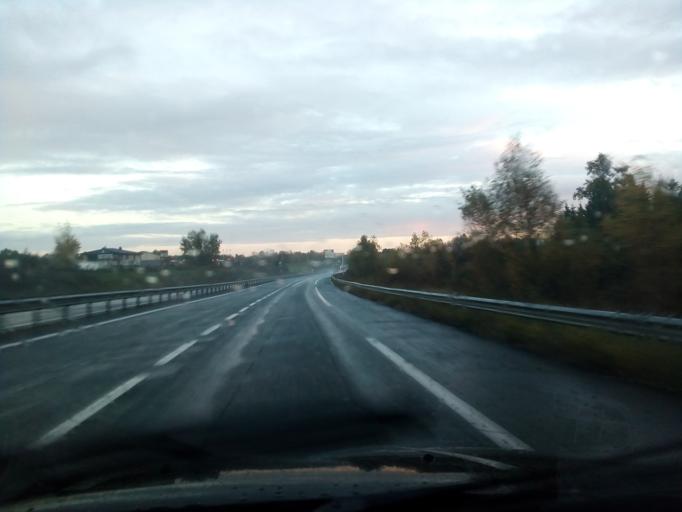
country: FR
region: Aquitaine
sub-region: Departement de la Gironde
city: Cavignac
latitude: 45.1074
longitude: -0.3801
